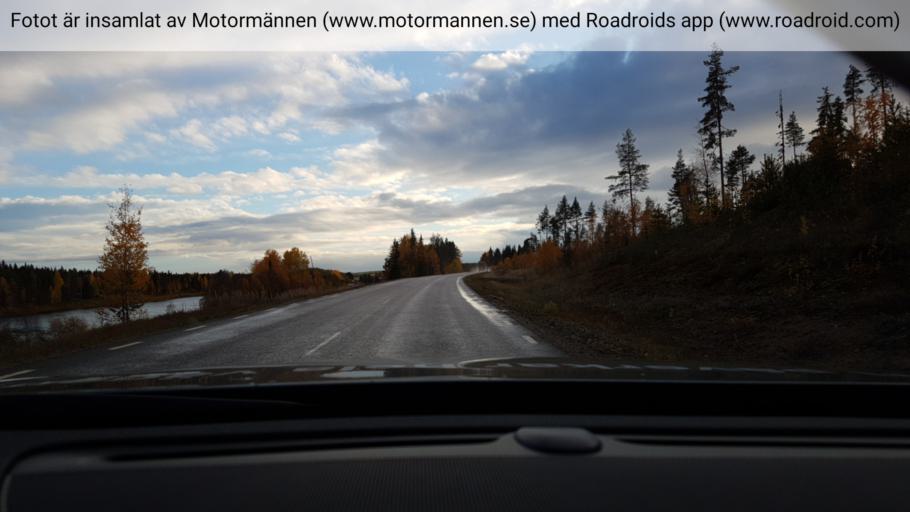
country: SE
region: Norrbotten
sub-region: Overkalix Kommun
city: OEverkalix
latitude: 66.7701
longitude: 22.6898
